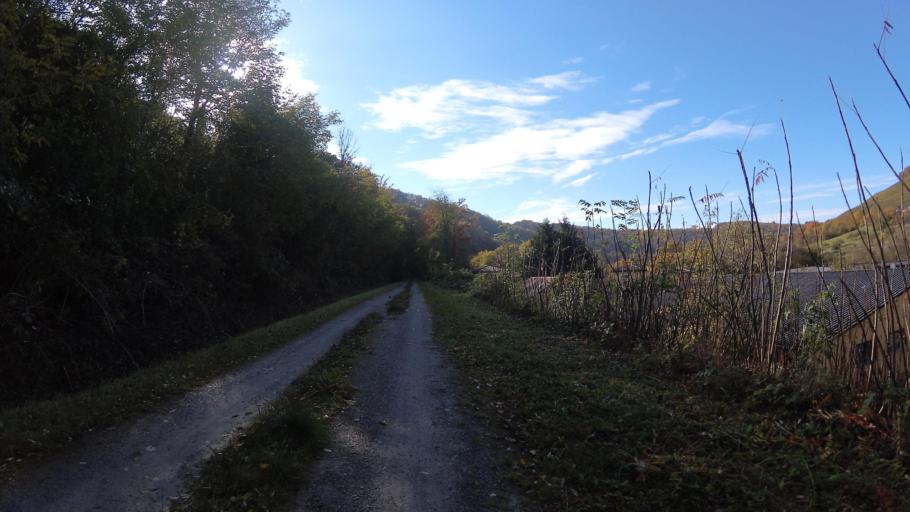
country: DE
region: Baden-Wuerttemberg
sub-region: Regierungsbezirk Stuttgart
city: Niedernhall
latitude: 49.2908
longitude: 9.6155
